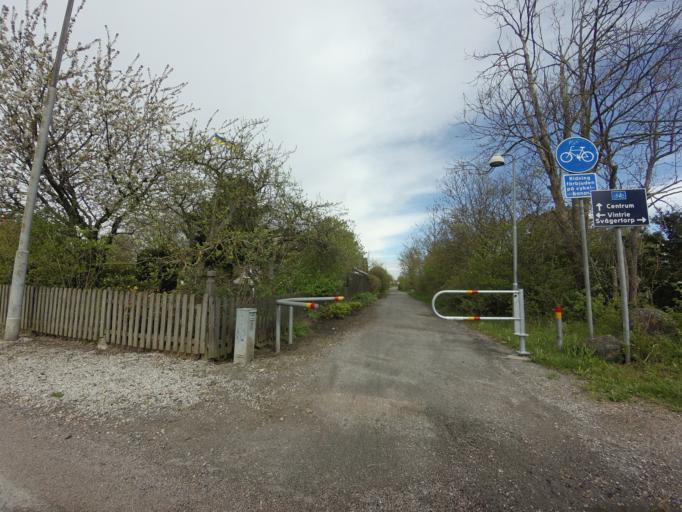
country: SE
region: Skane
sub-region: Malmo
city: Bunkeflostrand
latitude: 55.5513
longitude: 12.9663
